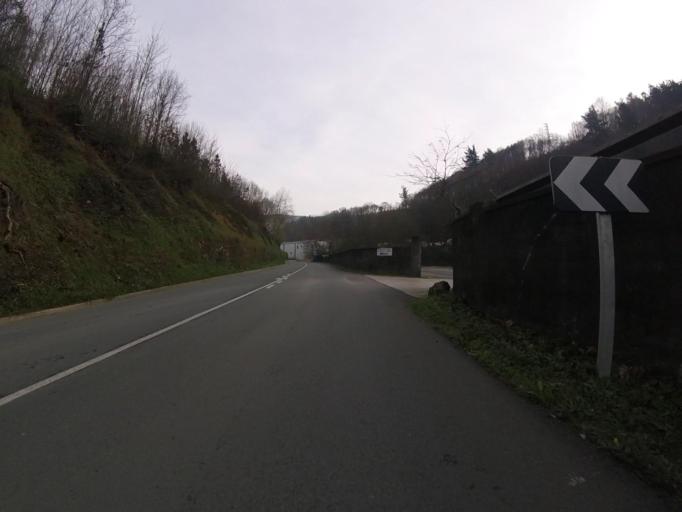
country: ES
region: Basque Country
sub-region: Provincia de Guipuzcoa
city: Berrobi
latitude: 43.1419
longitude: -2.0371
